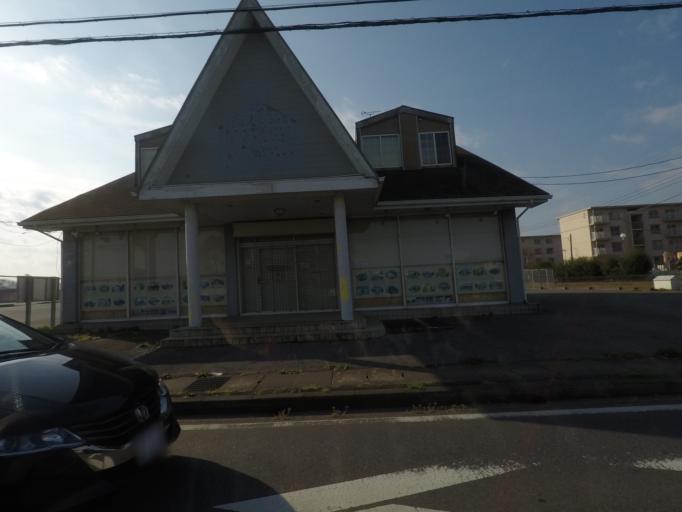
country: JP
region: Chiba
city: Yachimata
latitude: 35.6528
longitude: 140.3000
